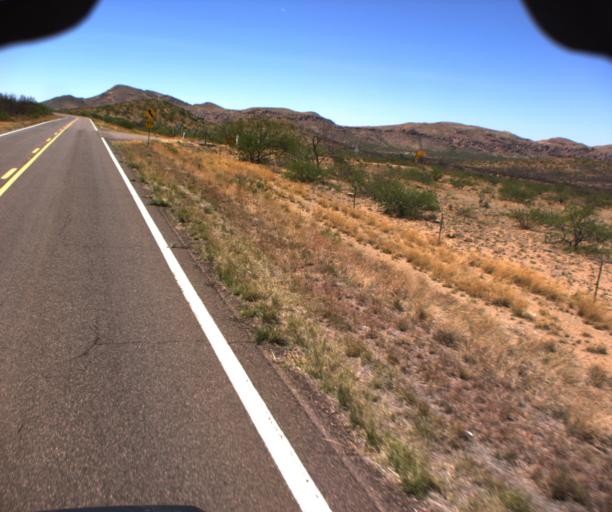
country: US
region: Arizona
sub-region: Cochise County
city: Douglas
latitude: 31.4873
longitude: -109.4371
